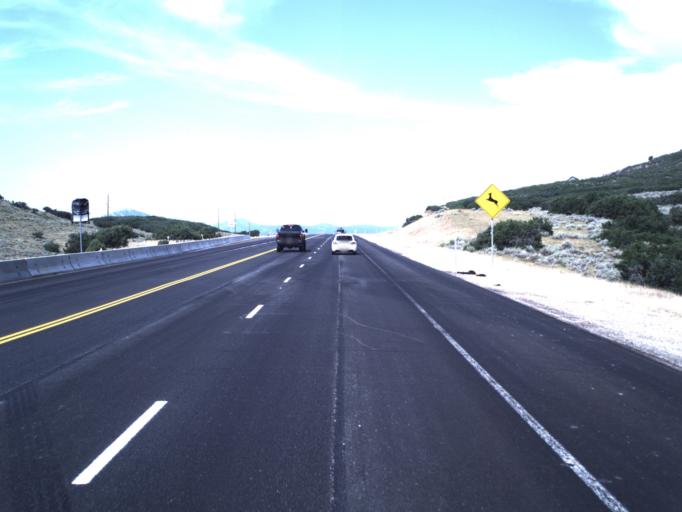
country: US
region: Utah
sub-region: Summit County
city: Kamas
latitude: 40.6346
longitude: -111.3654
